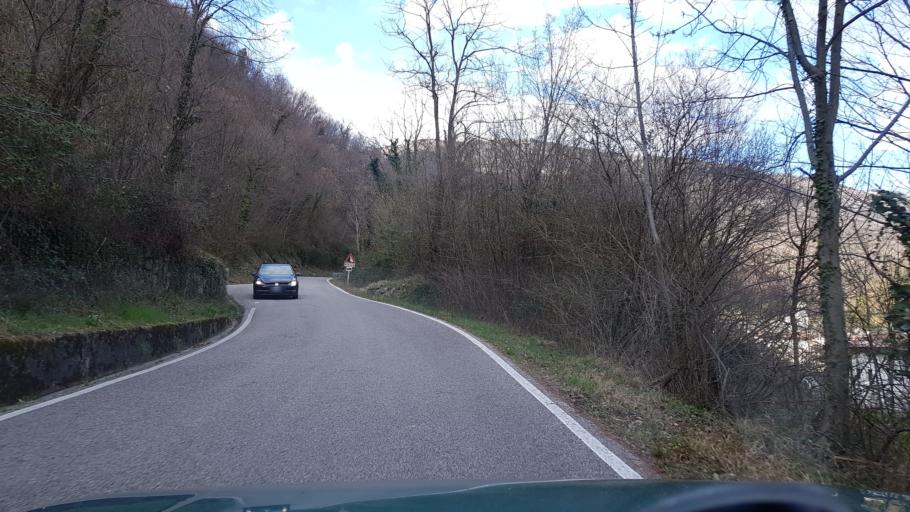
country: IT
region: Friuli Venezia Giulia
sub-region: Provincia di Udine
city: Faedis
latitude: 46.1647
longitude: 13.3576
